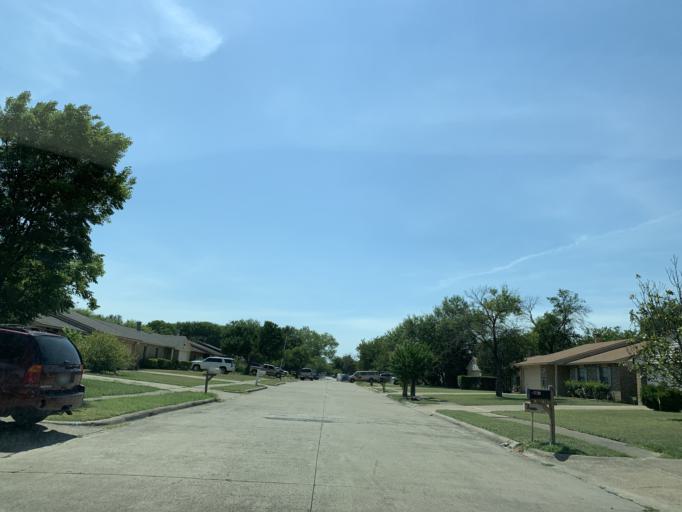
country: US
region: Texas
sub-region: Dallas County
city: Cedar Hill
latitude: 32.6523
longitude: -97.0183
